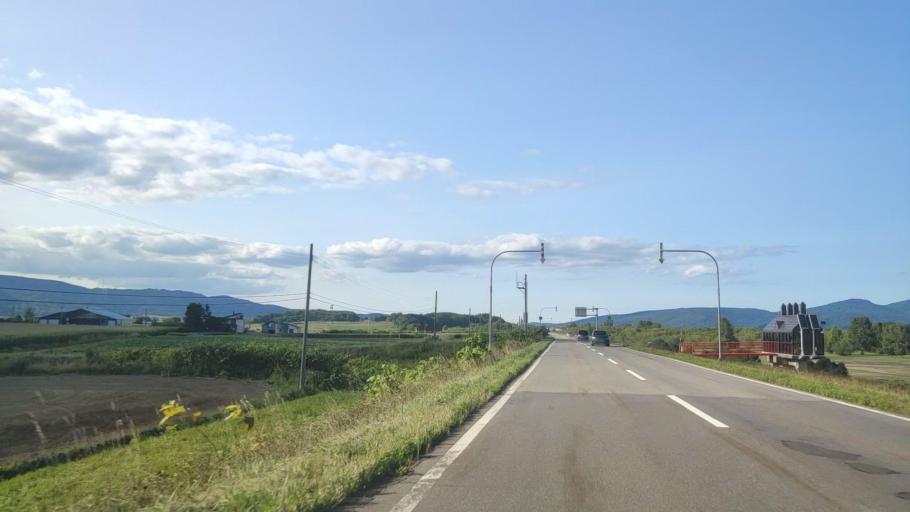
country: JP
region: Hokkaido
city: Nayoro
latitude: 44.8043
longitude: 142.0674
